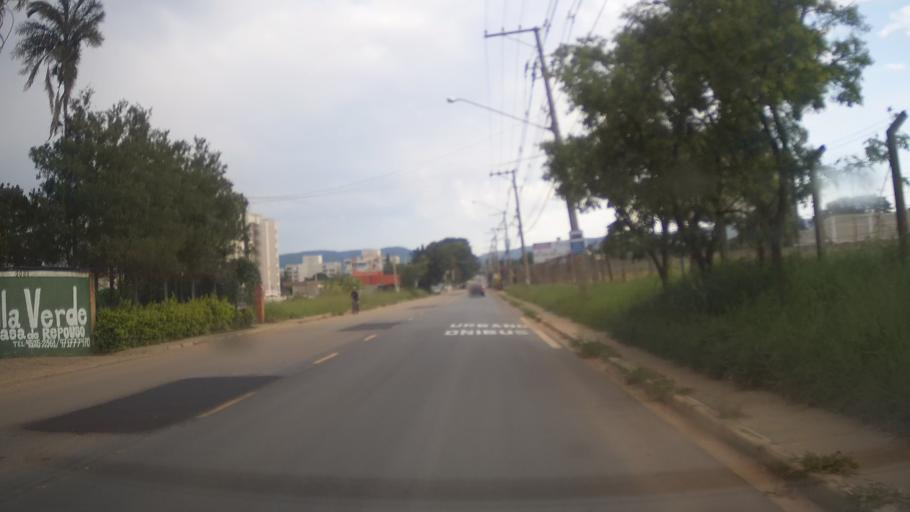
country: BR
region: Sao Paulo
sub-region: Itupeva
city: Itupeva
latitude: -23.1711
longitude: -47.0025
